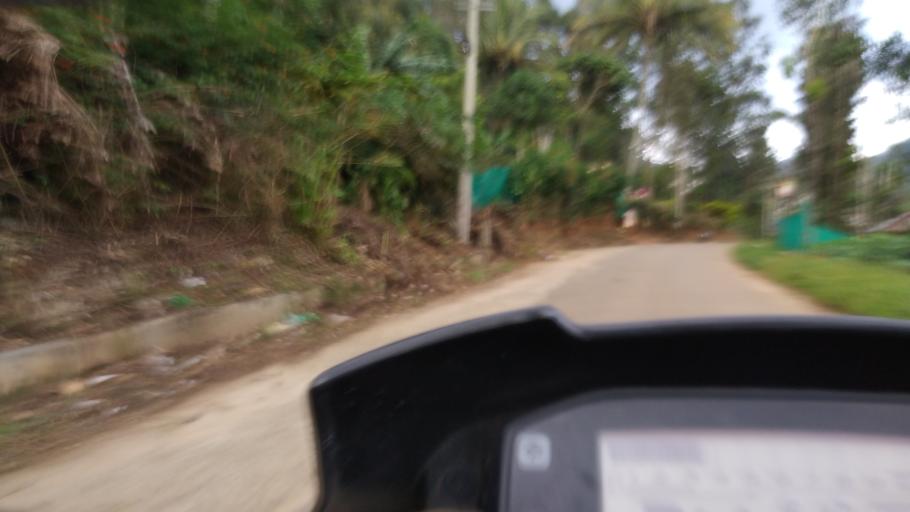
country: IN
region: Tamil Nadu
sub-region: Theni
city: Bodinayakkanur
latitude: 10.0243
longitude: 77.2383
